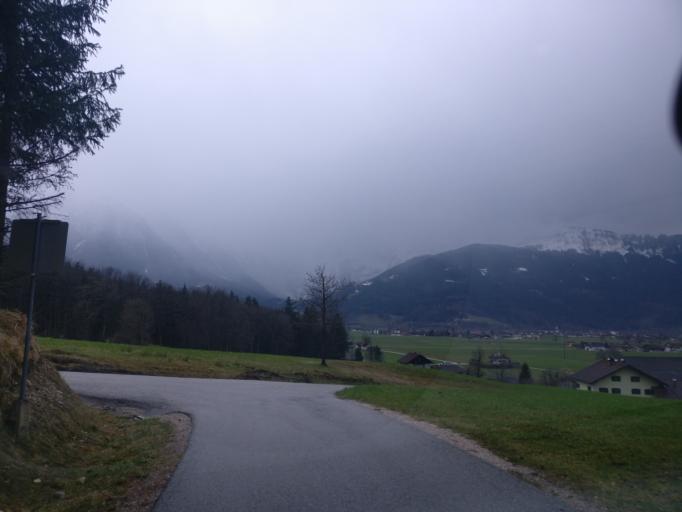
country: AT
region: Salzburg
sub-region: Politischer Bezirk Hallein
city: Golling an der Salzach
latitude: 47.6244
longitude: 13.1774
